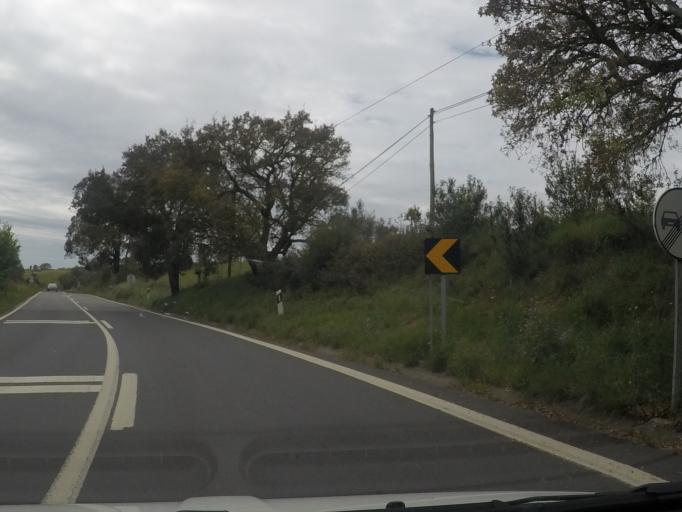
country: PT
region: Setubal
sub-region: Sines
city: Porto Covo
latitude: 37.8677
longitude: -8.7232
